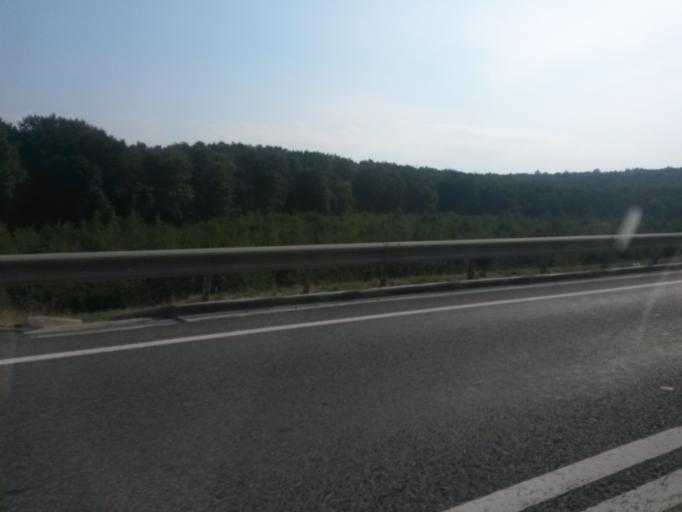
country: RO
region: Cluj
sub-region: Comuna Feleacu
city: Gheorghieni
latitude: 46.7109
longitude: 23.6565
